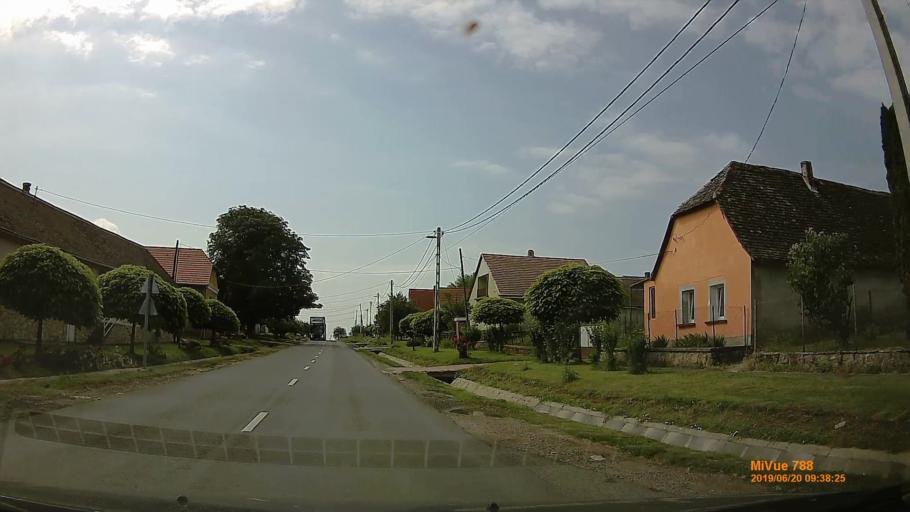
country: HU
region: Baranya
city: Pecsvarad
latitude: 46.1567
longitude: 18.4735
